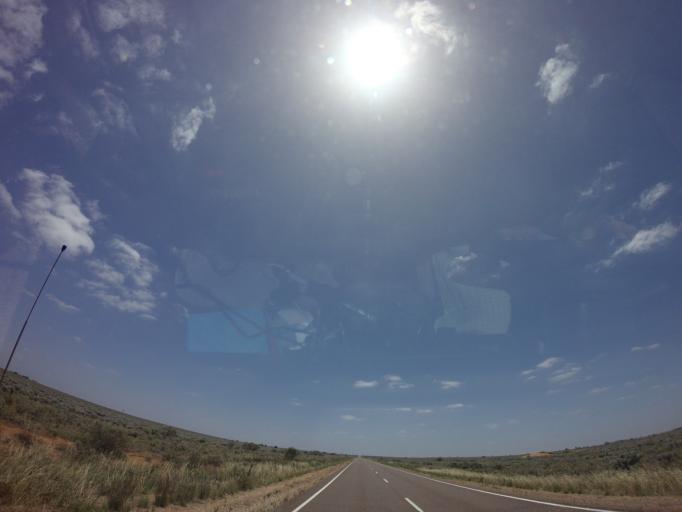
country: AU
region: South Australia
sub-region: Whyalla
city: Whyalla
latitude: -32.8518
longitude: 137.0166
